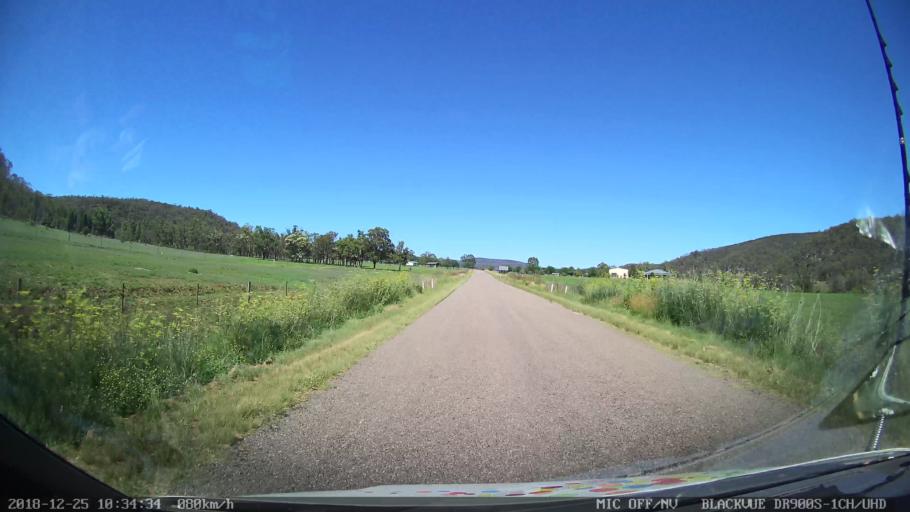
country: AU
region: New South Wales
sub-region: Upper Hunter Shire
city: Merriwa
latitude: -32.3928
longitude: 150.4064
